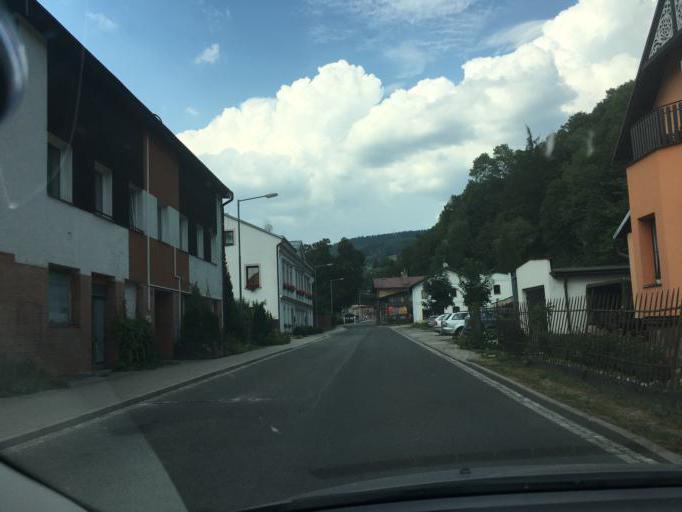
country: CZ
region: Kralovehradecky
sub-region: Okres Trutnov
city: Vrchlabi
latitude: 50.6370
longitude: 15.6075
